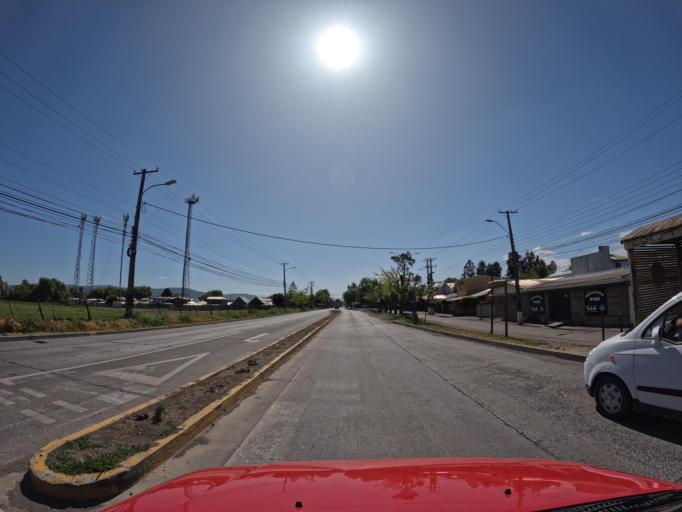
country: CL
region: Maule
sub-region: Provincia de Curico
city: Molina
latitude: -35.0607
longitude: -71.2628
